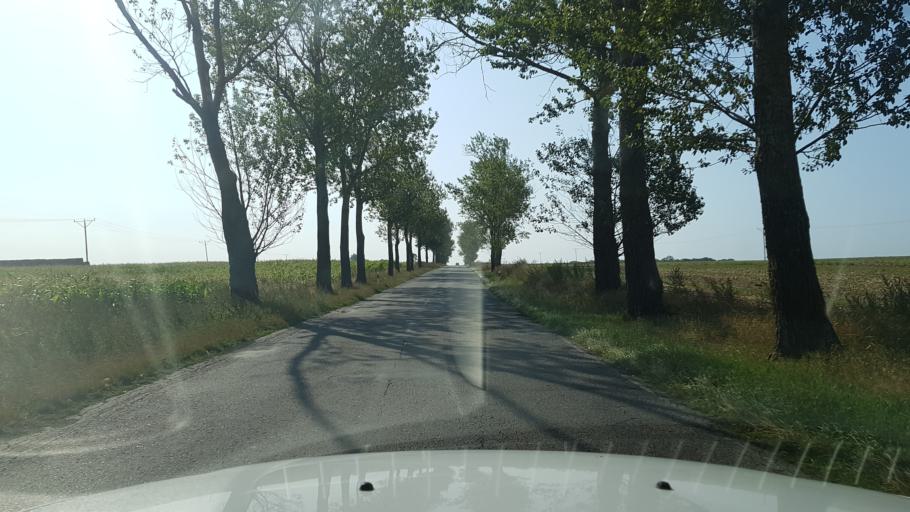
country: PL
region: West Pomeranian Voivodeship
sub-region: Powiat stargardzki
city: Stargard Szczecinski
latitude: 53.2710
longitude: 15.0874
